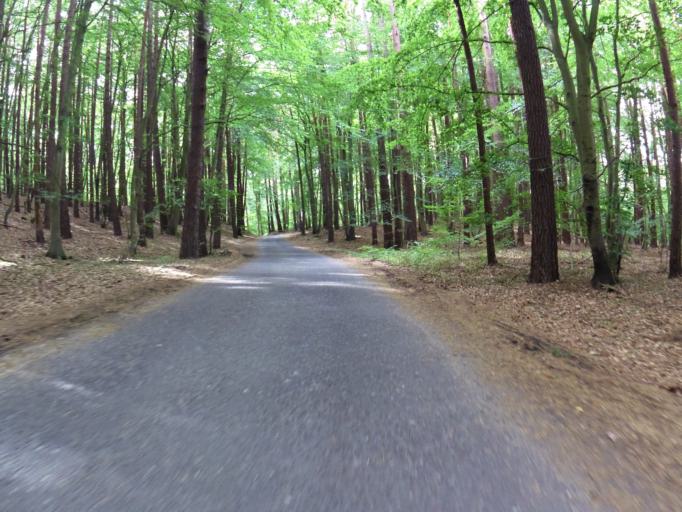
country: DE
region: Mecklenburg-Vorpommern
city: Seebad Bansin
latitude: 53.9793
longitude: 14.1076
